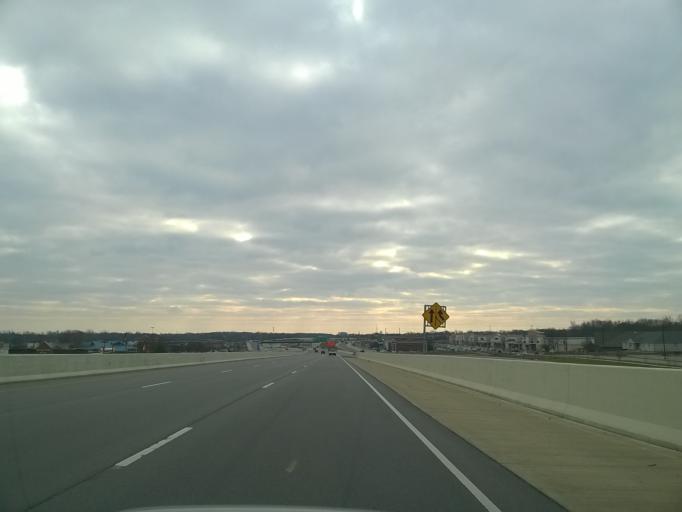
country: US
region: Indiana
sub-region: Hamilton County
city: Carmel
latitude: 40.0053
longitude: -86.1275
